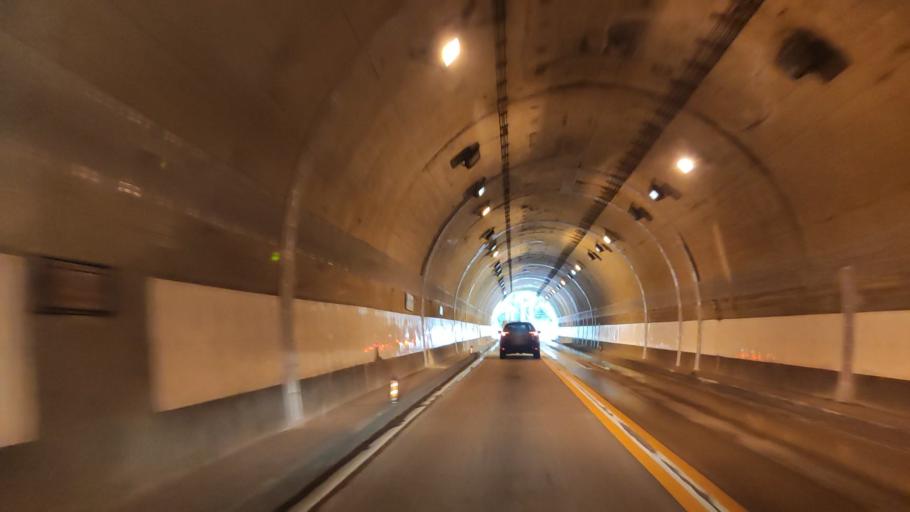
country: JP
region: Tokushima
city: Kamojimacho-jogejima
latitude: 34.1658
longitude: 134.3323
